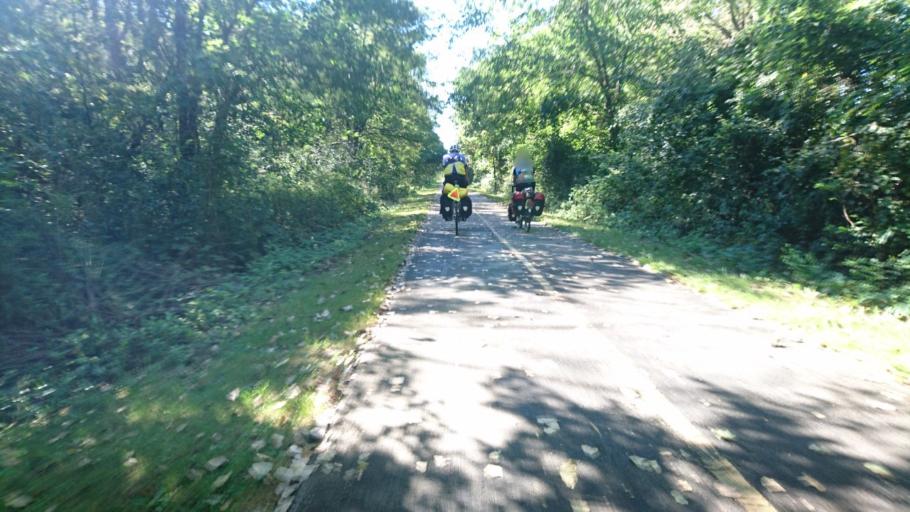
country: US
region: Indiana
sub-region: Lake County
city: Whiting
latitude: 41.6875
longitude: -87.5304
